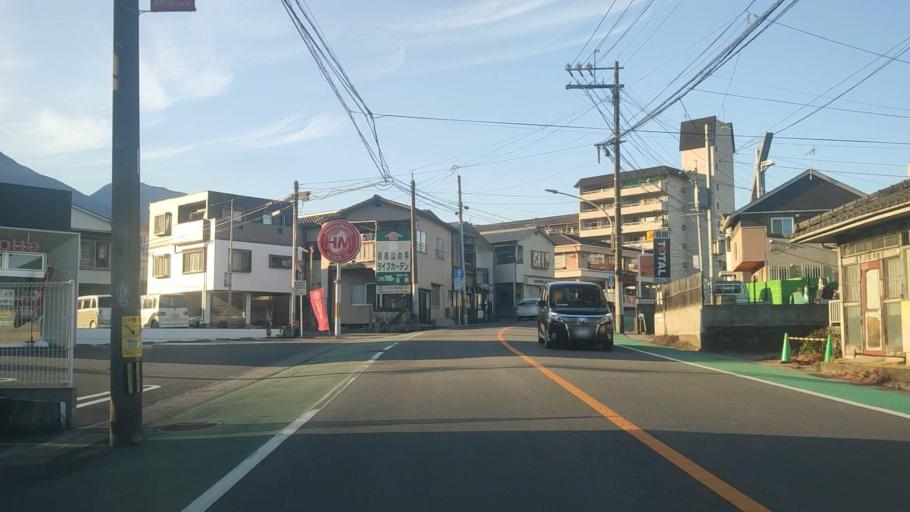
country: JP
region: Oita
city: Beppu
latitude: 33.2776
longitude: 131.4899
